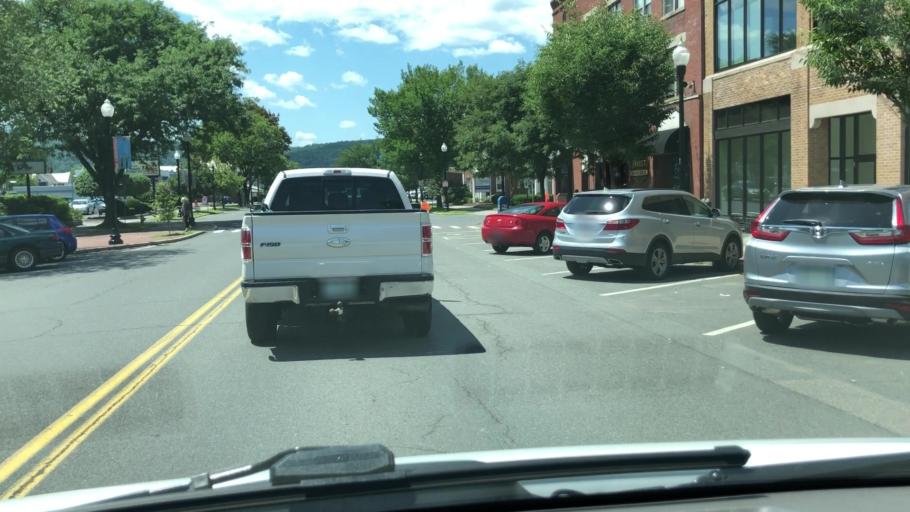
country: US
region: Massachusetts
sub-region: Franklin County
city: Greenfield
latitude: 42.5876
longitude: -72.6052
